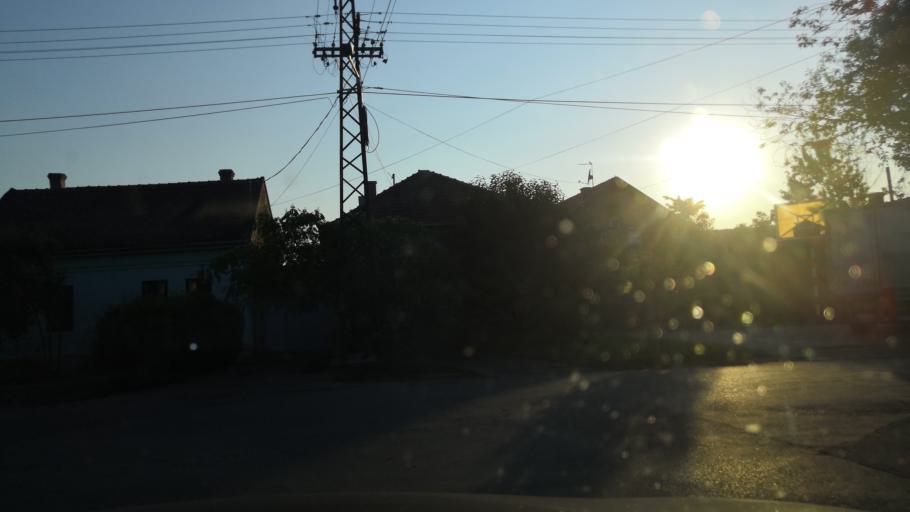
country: RS
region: Autonomna Pokrajina Vojvodina
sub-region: Sremski Okrug
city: Stara Pazova
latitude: 44.9904
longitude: 20.1625
